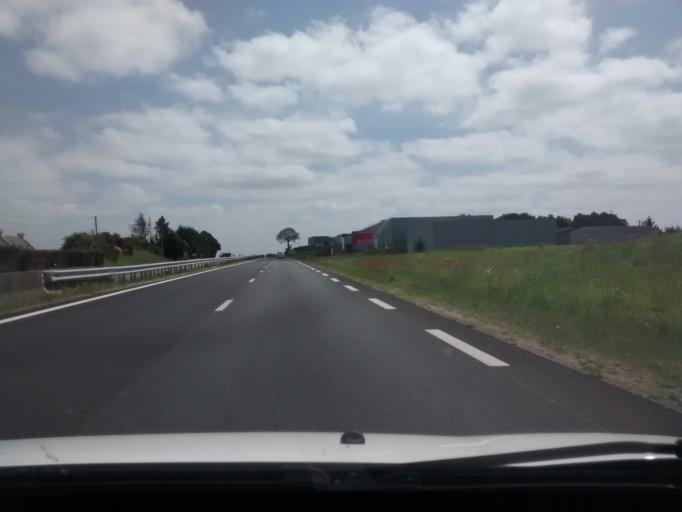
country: FR
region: Brittany
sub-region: Departement des Cotes-d'Armor
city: Cavan
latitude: 48.6909
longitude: -3.3686
